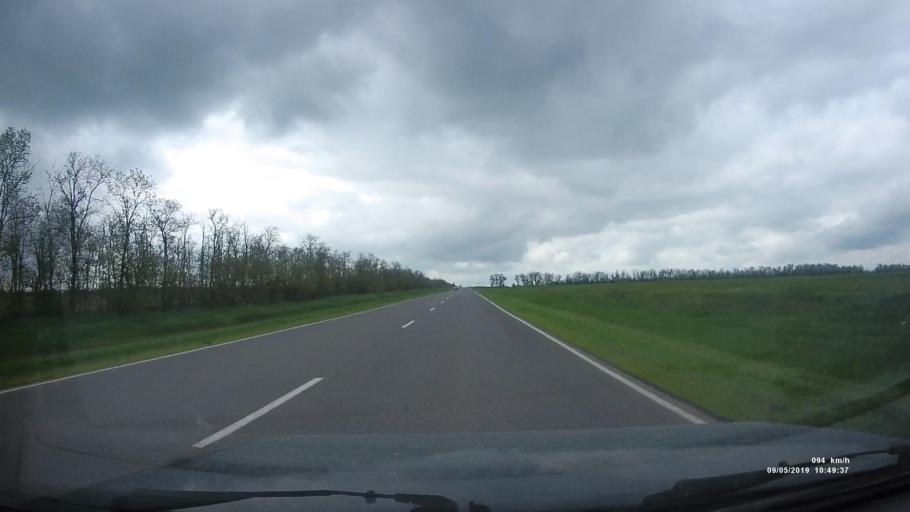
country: RU
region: Rostov
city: Peshkovo
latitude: 46.9399
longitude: 39.3557
